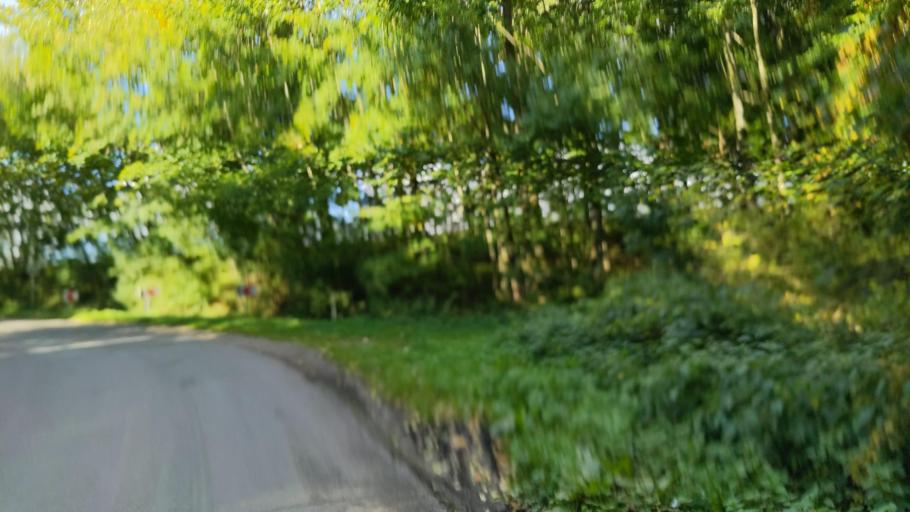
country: DE
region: Schleswig-Holstein
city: Ahrensbok
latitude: 53.9949
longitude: 10.5891
